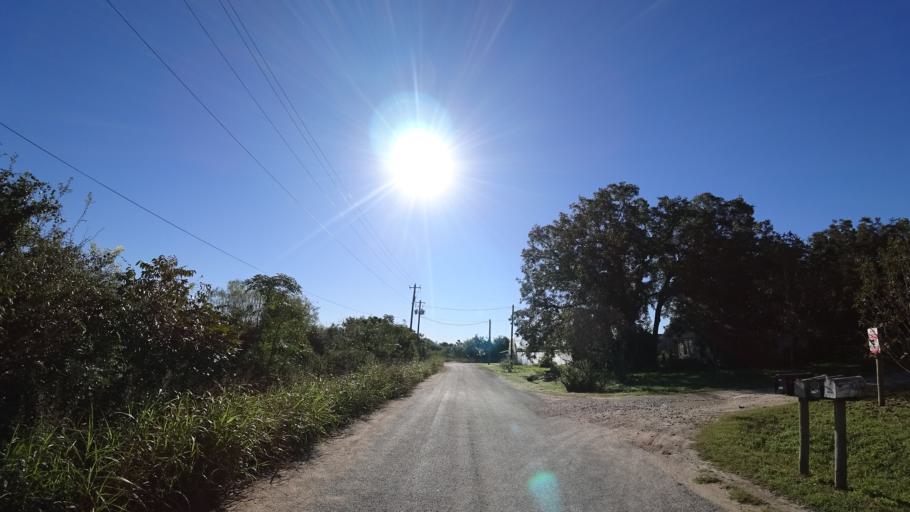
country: US
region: Texas
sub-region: Travis County
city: Hornsby Bend
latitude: 30.2374
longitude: -97.6542
